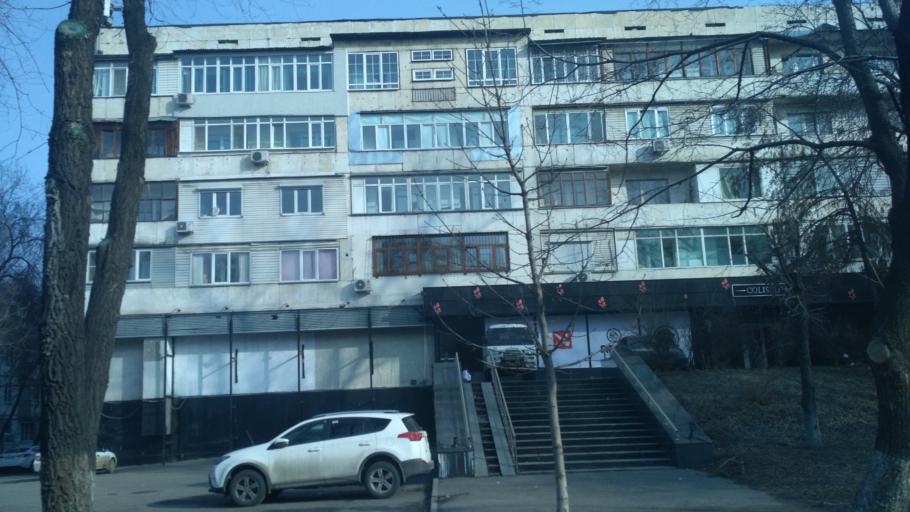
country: KZ
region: Almaty Qalasy
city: Almaty
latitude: 43.2269
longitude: 76.9204
